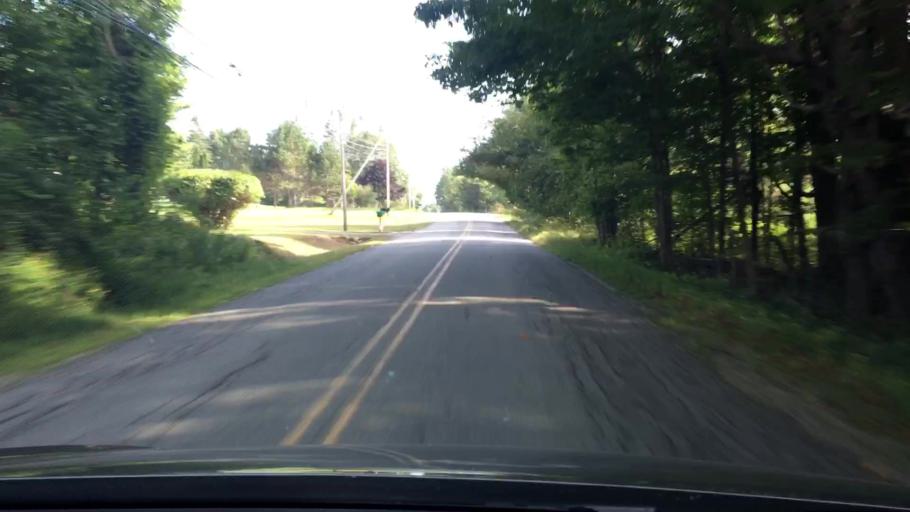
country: US
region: Maine
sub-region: Hancock County
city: Bucksport
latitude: 44.5472
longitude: -68.7973
